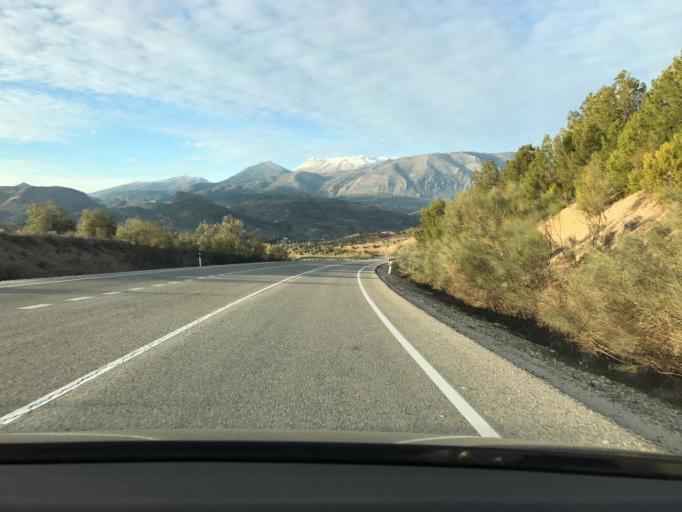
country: ES
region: Andalusia
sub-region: Provincia de Jaen
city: Huelma
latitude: 37.6358
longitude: -3.4099
